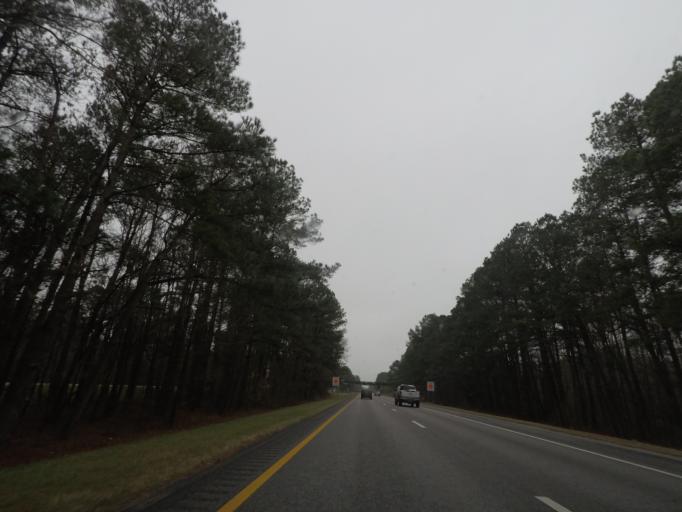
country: US
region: South Carolina
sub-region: Sumter County
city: East Sumter
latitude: 33.8885
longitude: -80.0987
